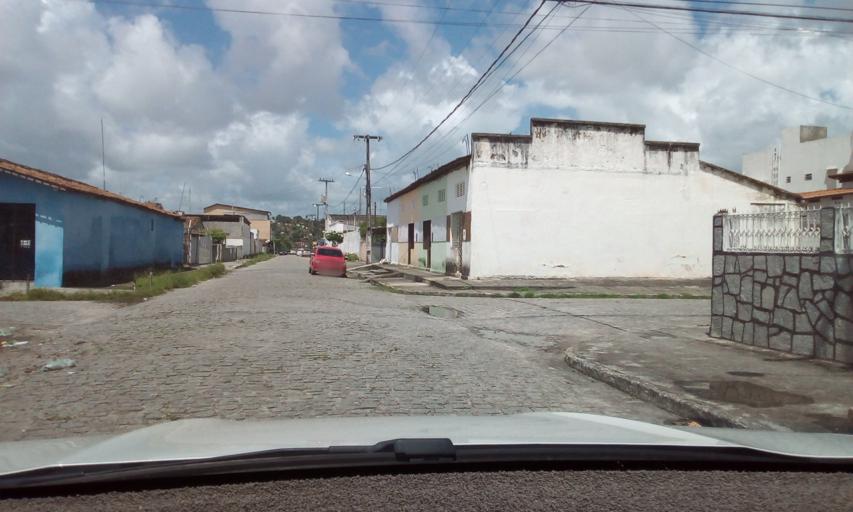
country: BR
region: Paraiba
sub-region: Bayeux
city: Bayeux
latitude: -7.1237
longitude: -34.9174
